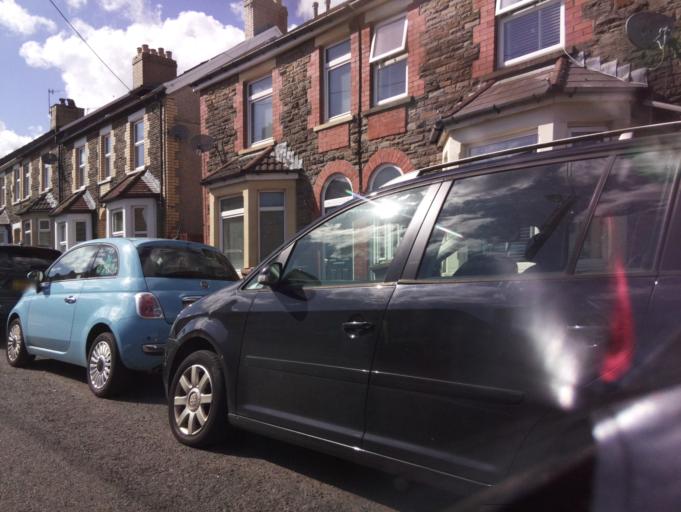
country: GB
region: Wales
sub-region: Caerphilly County Borough
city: Caerphilly
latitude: 51.5736
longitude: -3.2112
